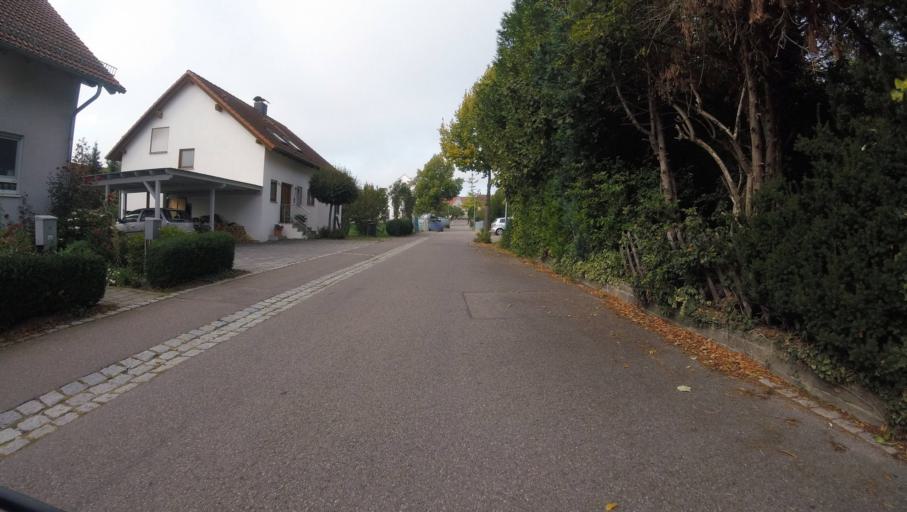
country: DE
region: Baden-Wuerttemberg
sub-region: Regierungsbezirk Stuttgart
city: Motzingen
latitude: 48.5346
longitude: 8.7783
